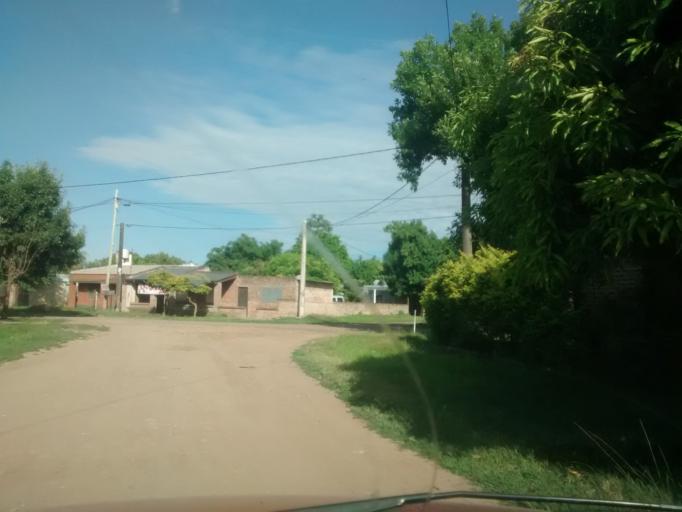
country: AR
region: Chaco
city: Puerto Tirol
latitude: -27.3736
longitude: -59.0940
